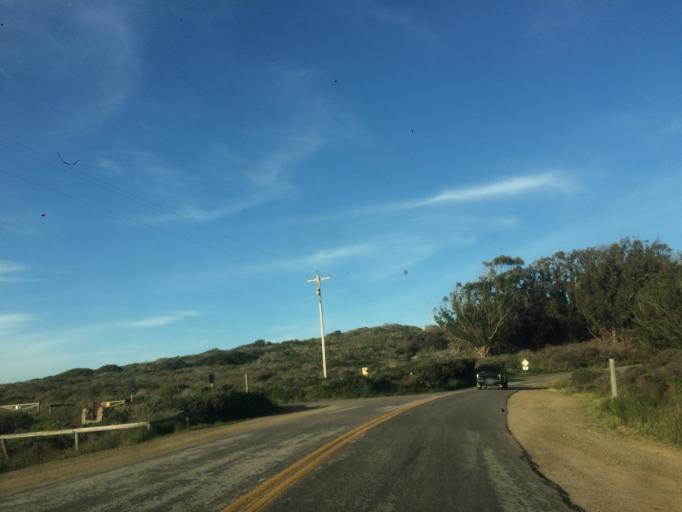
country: US
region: California
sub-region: San Luis Obispo County
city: Los Osos
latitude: 35.2941
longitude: -120.8721
